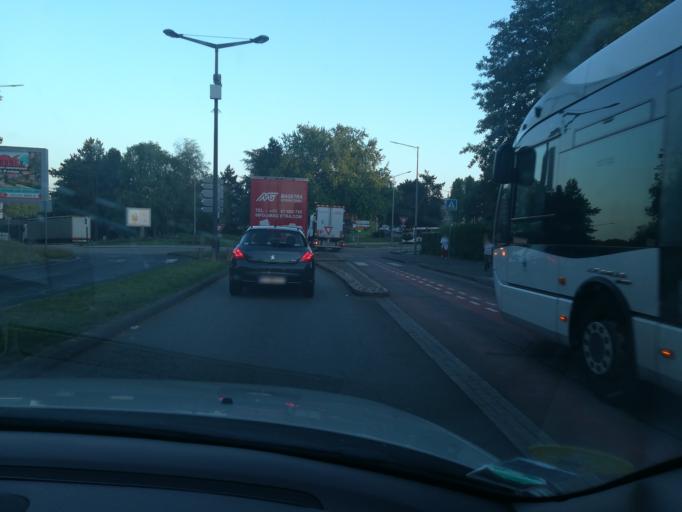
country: FR
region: Haute-Normandie
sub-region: Departement de la Seine-Maritime
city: Bois-Guillaume
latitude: 49.4621
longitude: 1.1314
